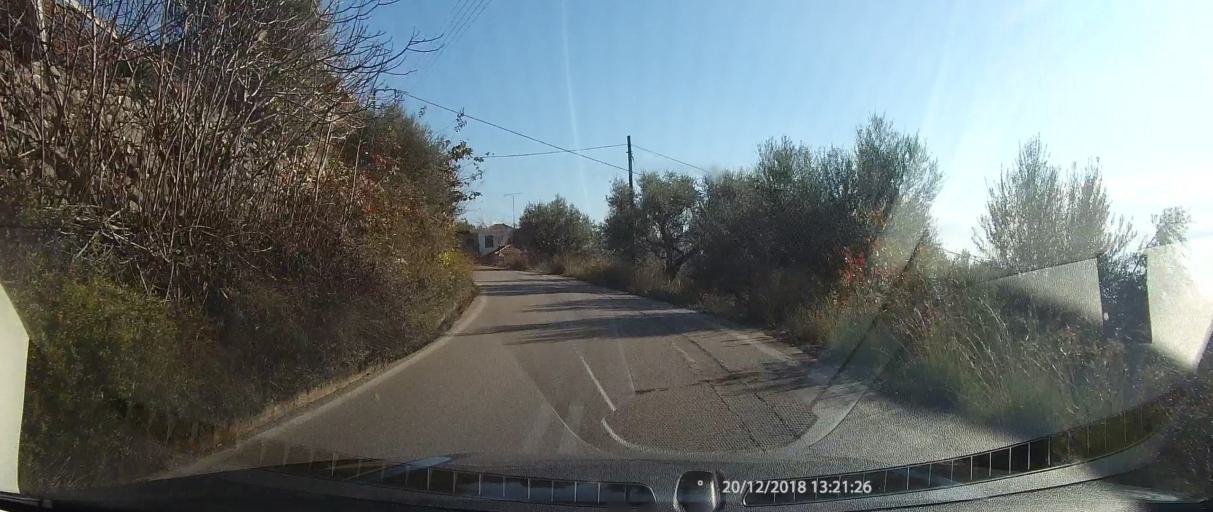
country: GR
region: West Greece
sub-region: Nomos Aitolias kai Akarnanias
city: Paravola
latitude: 38.6170
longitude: 21.5554
